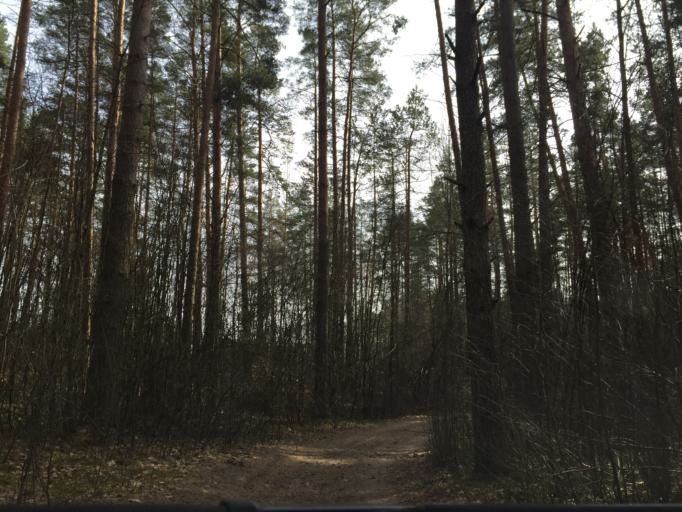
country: LV
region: Kekava
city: Balozi
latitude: 56.8830
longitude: 24.1400
